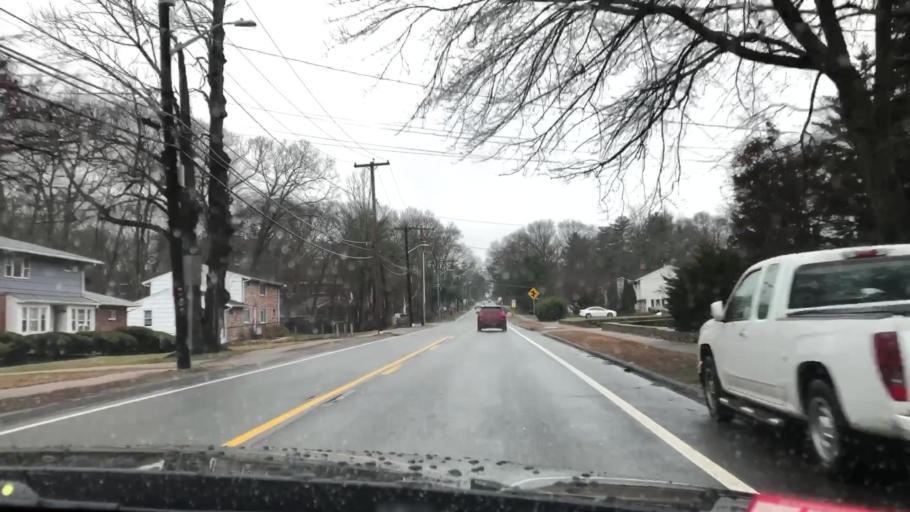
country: US
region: Massachusetts
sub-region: Norfolk County
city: Norwood
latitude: 42.1746
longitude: -71.2241
